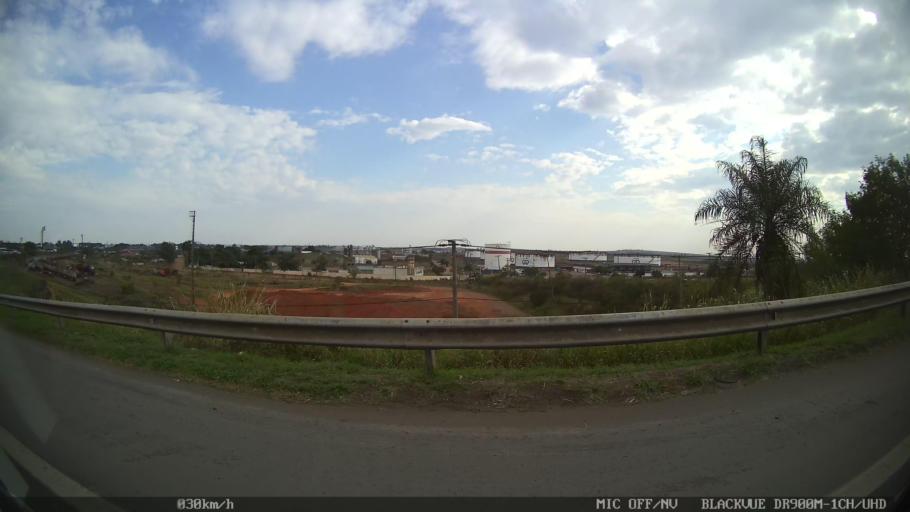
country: BR
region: Sao Paulo
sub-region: Paulinia
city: Paulinia
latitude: -22.7117
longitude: -47.1436
